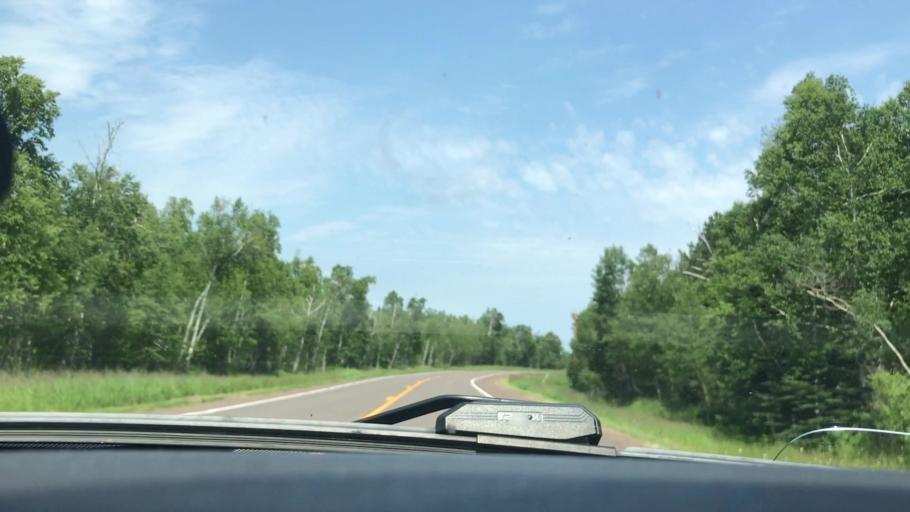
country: US
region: Minnesota
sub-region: Lake County
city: Silver Bay
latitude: 47.4920
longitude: -90.9800
